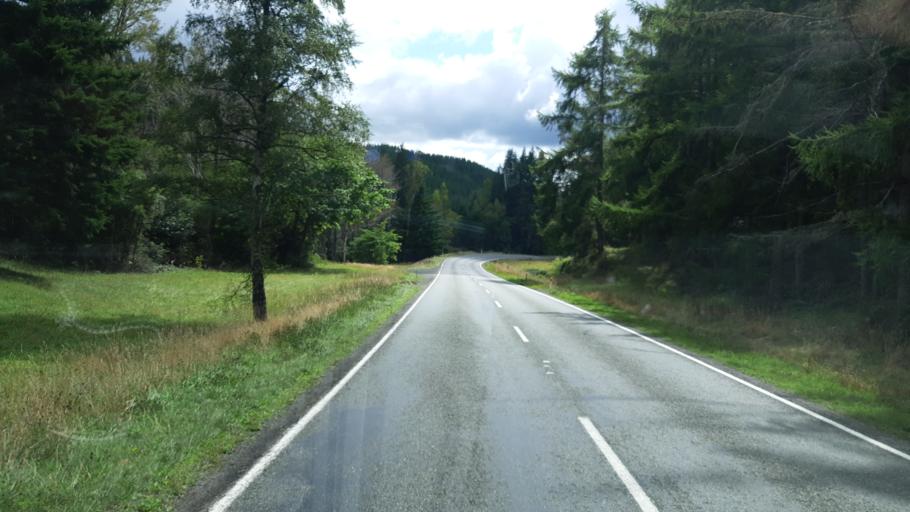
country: NZ
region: Tasman
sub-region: Tasman District
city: Wakefield
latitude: -41.6045
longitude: 172.7590
